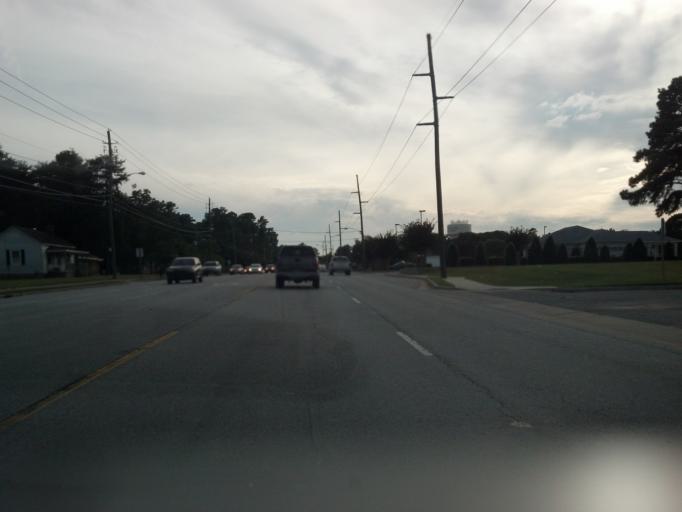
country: US
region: North Carolina
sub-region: Pitt County
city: Greenville
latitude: 35.5934
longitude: -77.3411
